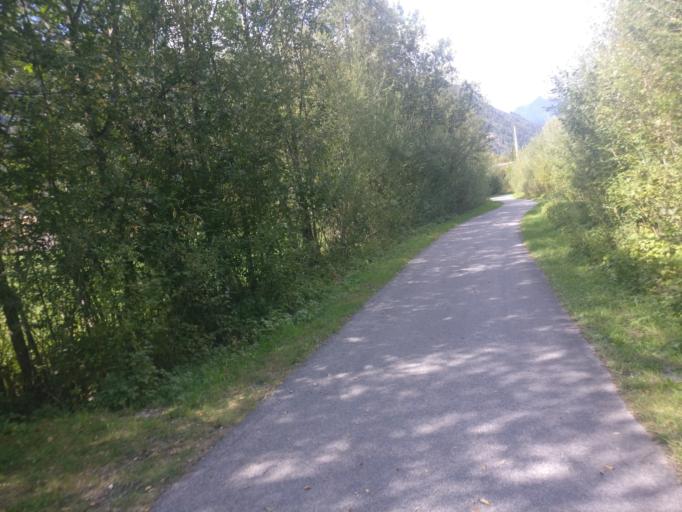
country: AT
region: Salzburg
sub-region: Politischer Bezirk Sankt Johann im Pongau
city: Bischofshofen
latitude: 47.4233
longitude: 13.2236
